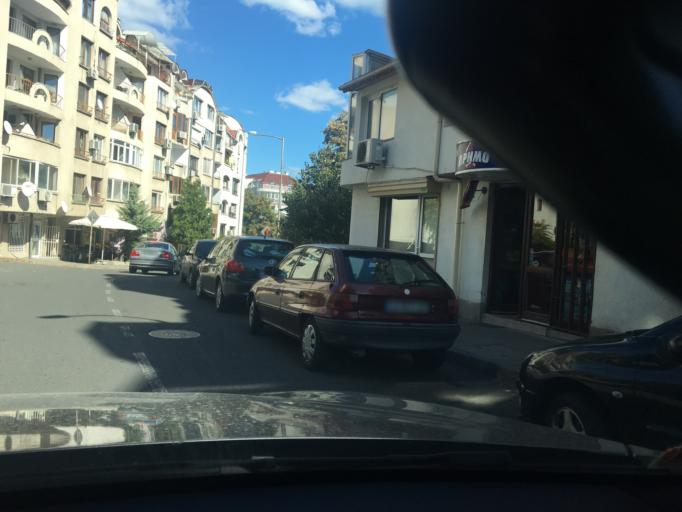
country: BG
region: Burgas
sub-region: Obshtina Burgas
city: Burgas
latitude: 42.5095
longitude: 27.4742
